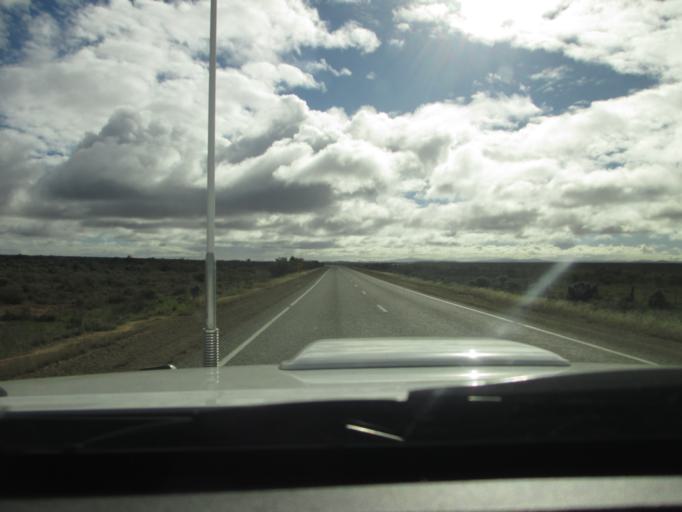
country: AU
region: South Australia
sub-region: Flinders Ranges
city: Quorn
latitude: -32.1817
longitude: 138.5382
